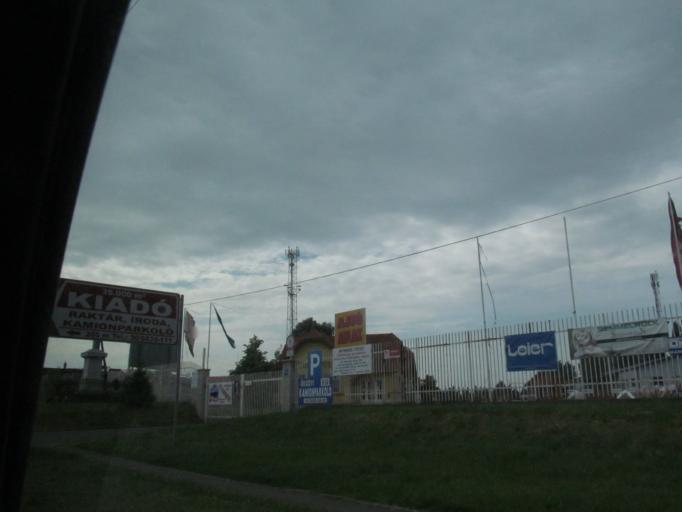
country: HU
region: Szabolcs-Szatmar-Bereg
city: Nyiregyhaza
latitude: 47.9396
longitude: 21.7458
